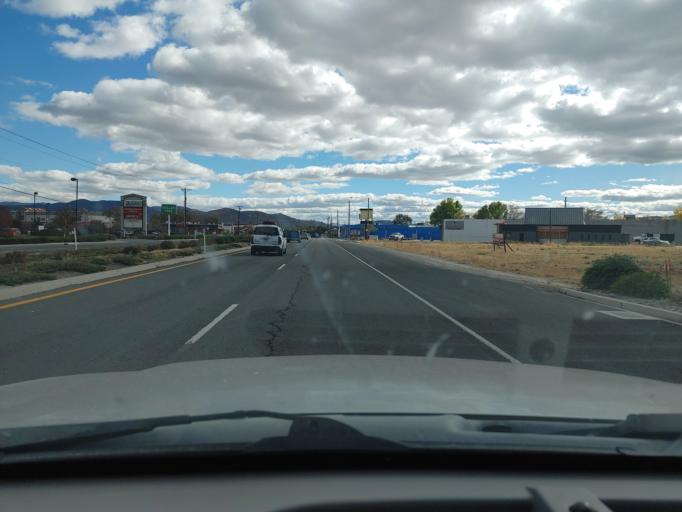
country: US
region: Nevada
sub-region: Carson City
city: Carson City
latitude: 39.1847
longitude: -119.7697
